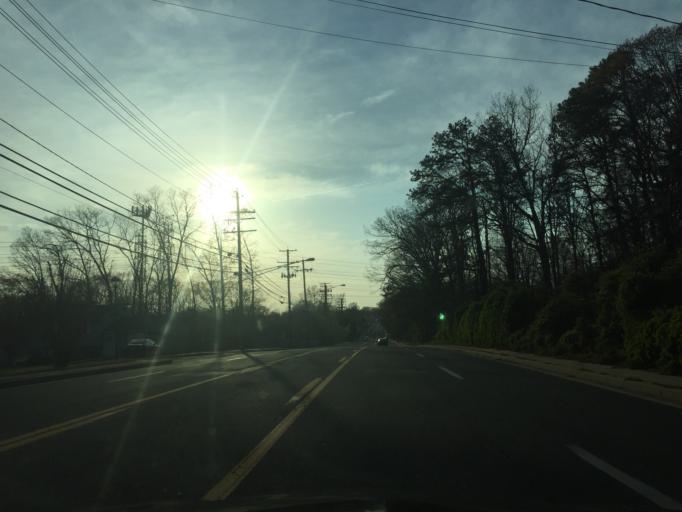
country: US
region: Maryland
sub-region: Baltimore County
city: Perry Hall
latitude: 39.3885
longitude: -76.4738
